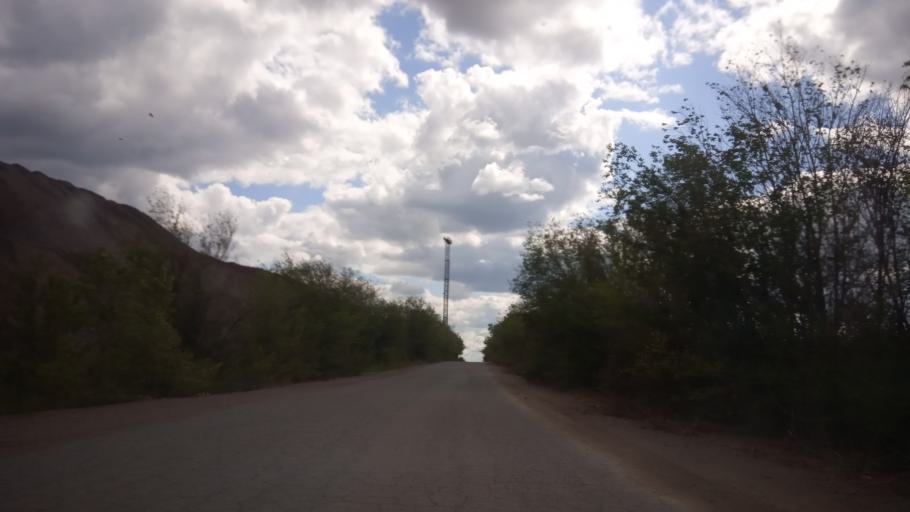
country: RU
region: Orenburg
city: Novotroitsk
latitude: 51.2518
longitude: 58.3659
